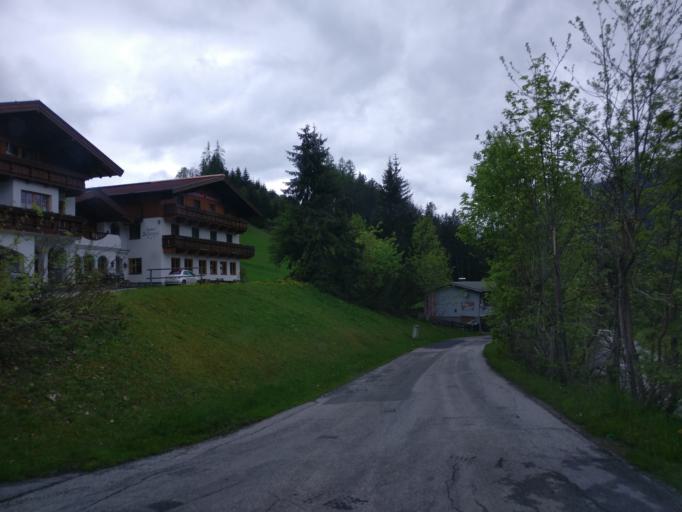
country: AT
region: Salzburg
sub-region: Politischer Bezirk Sankt Johann im Pongau
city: Werfenweng
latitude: 47.4569
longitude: 13.2698
